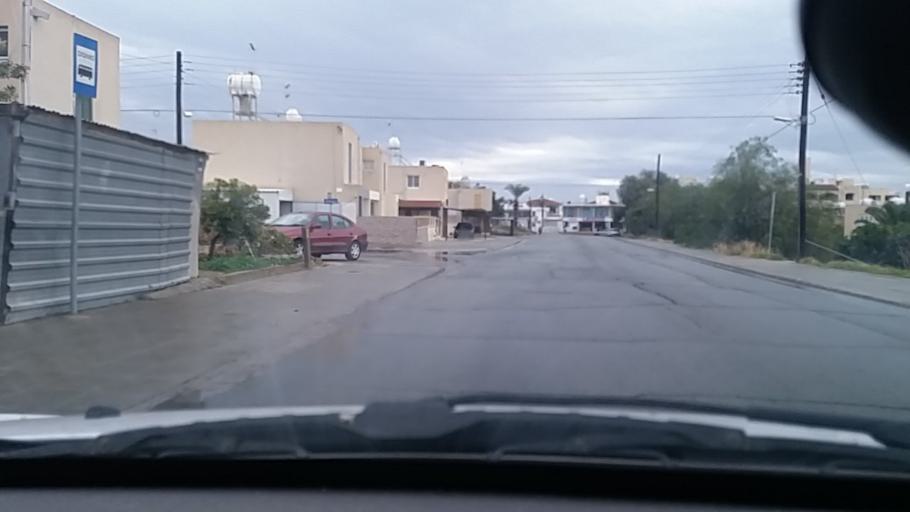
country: CY
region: Larnaka
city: Livadia
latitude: 34.9372
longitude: 33.6243
